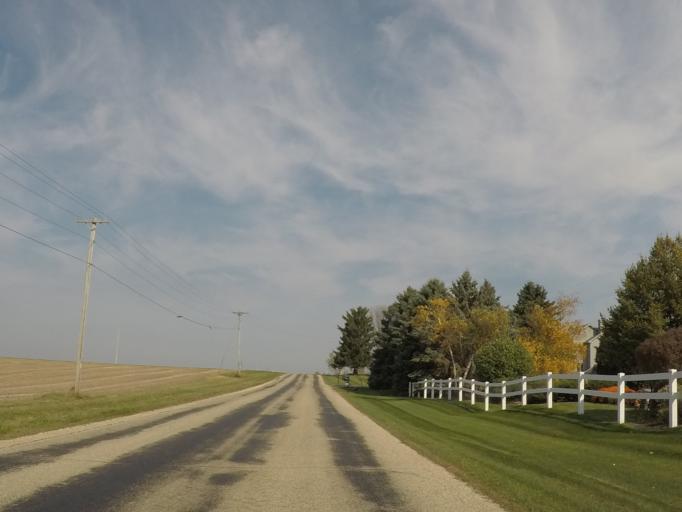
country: US
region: Wisconsin
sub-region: Dane County
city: Cross Plains
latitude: 43.0503
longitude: -89.6010
